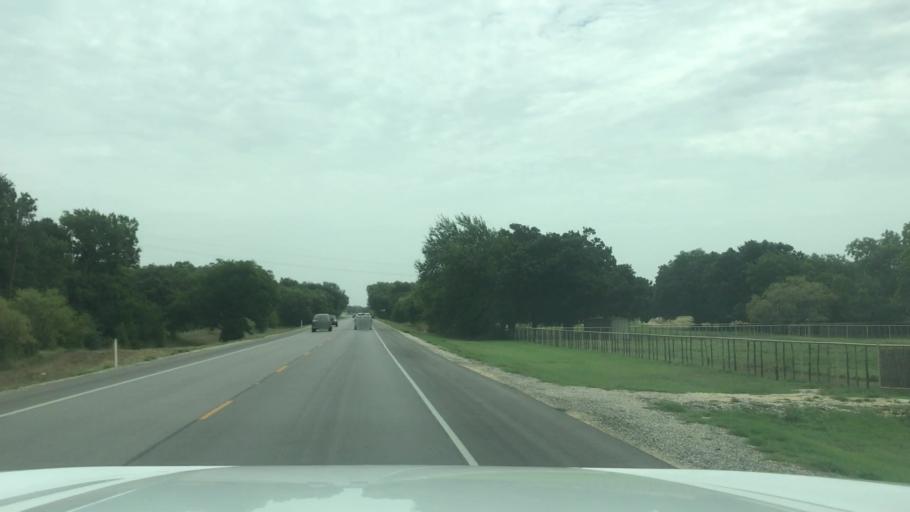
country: US
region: Texas
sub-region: Erath County
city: Dublin
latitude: 32.0882
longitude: -98.3002
